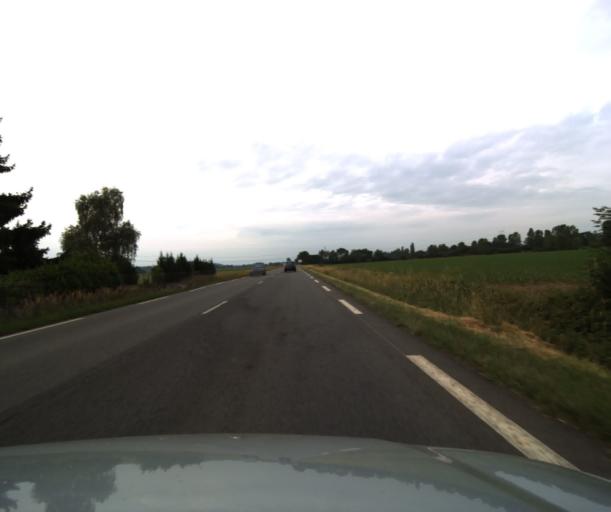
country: FR
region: Midi-Pyrenees
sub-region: Departement des Hautes-Pyrenees
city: Rabastens-de-Bigorre
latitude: 43.3769
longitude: 0.1468
